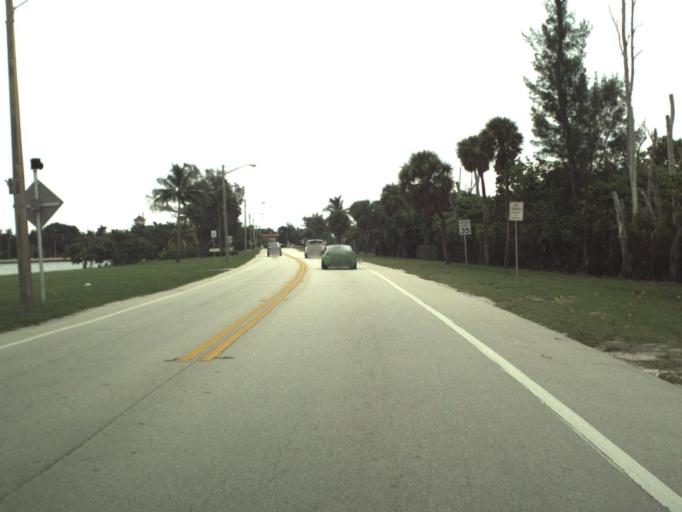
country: US
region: Florida
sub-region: Palm Beach County
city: Palm Beach
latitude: 26.6753
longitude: -80.0443
